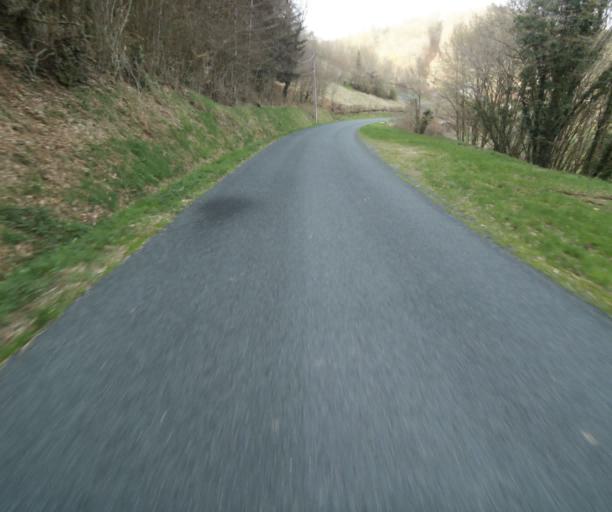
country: FR
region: Limousin
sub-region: Departement de la Correze
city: Naves
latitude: 45.3358
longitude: 1.7910
